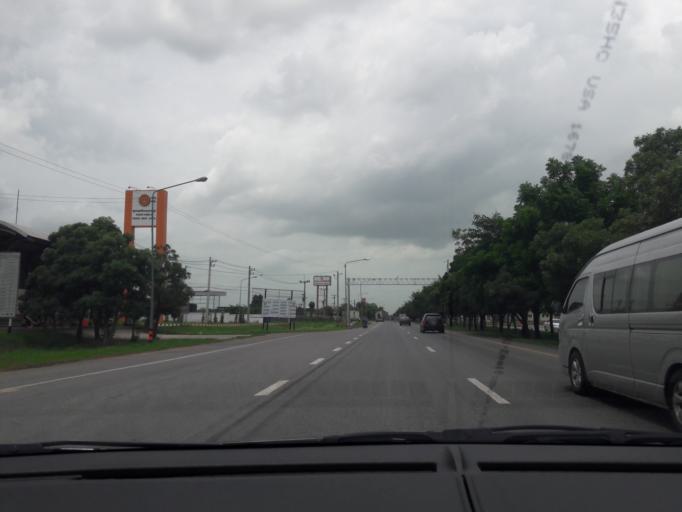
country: TH
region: Nakhon Ratchasima
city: Non Sung
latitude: 15.0920
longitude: 102.2466
